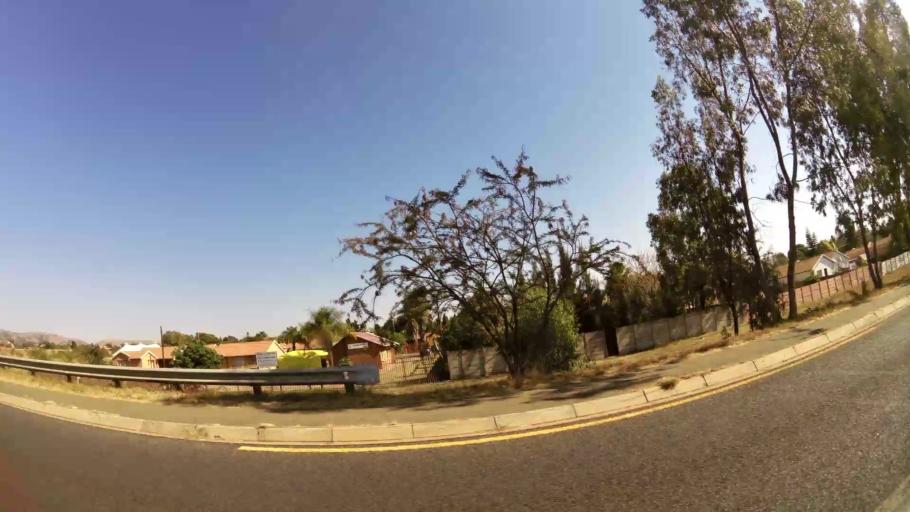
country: ZA
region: North-West
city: Ga-Rankuwa
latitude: -25.6539
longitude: 28.1021
